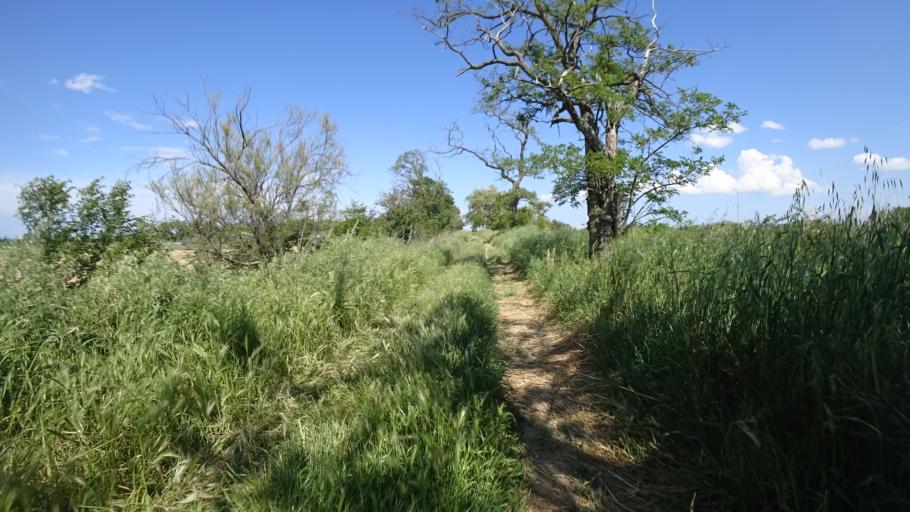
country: FR
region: Languedoc-Roussillon
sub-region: Departement de l'Aude
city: Ginestas
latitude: 43.2575
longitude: 2.8935
